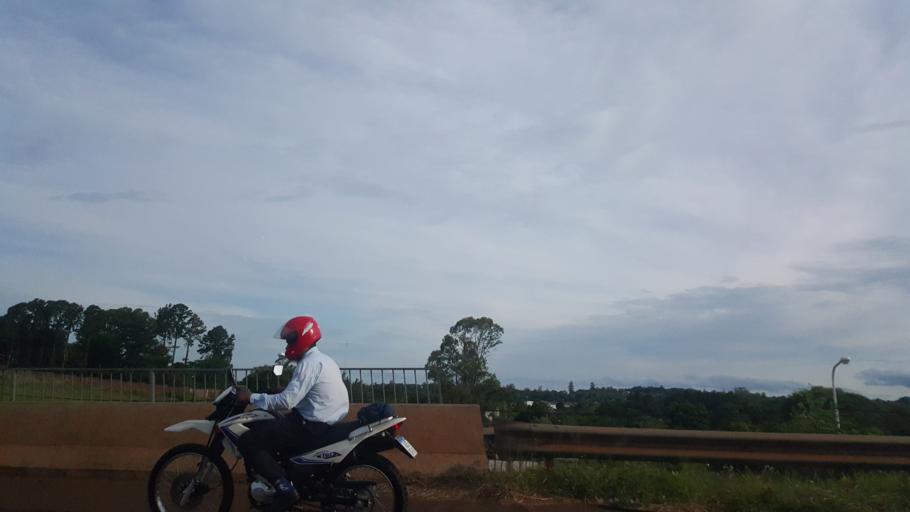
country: AR
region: Misiones
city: Garupa
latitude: -27.4518
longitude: -55.8575
